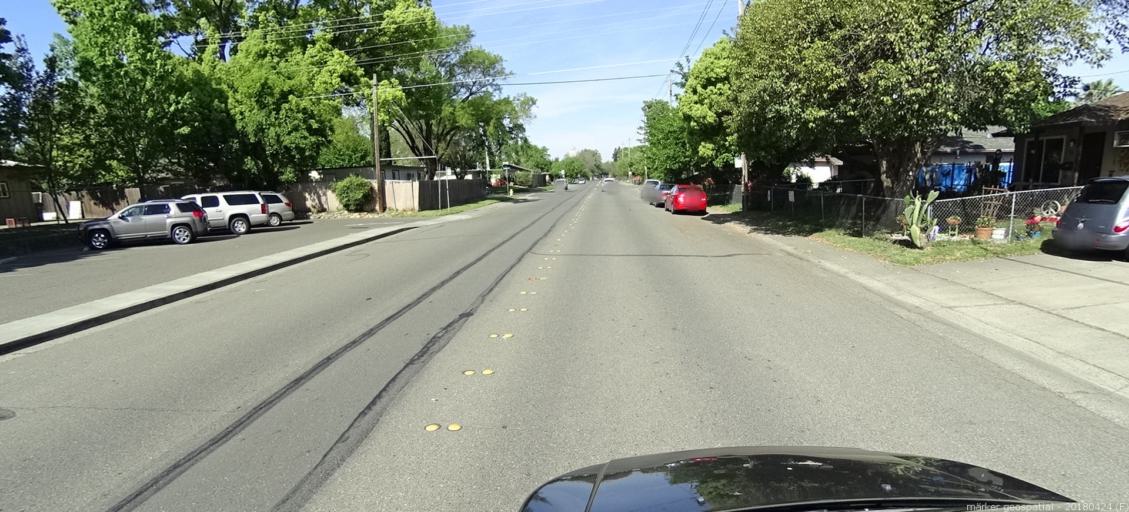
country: US
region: California
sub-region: Yolo County
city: West Sacramento
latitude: 38.5631
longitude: -121.5309
